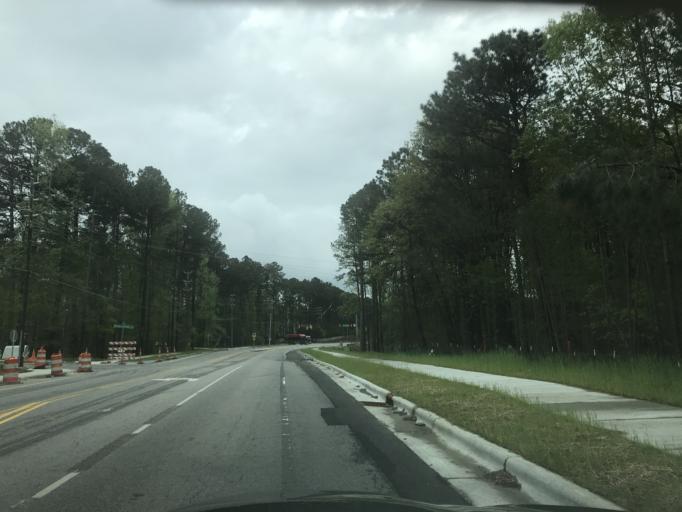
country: US
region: North Carolina
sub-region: Wake County
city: West Raleigh
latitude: 35.7526
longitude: -78.6946
